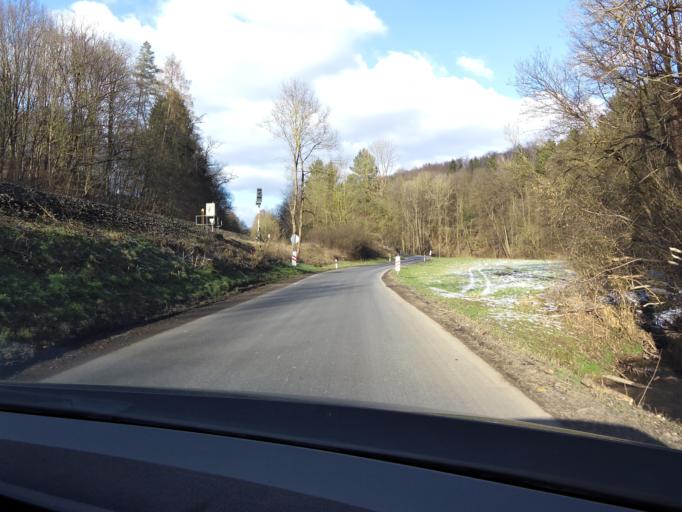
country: DE
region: Thuringia
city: Leimbach
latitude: 50.8399
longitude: 10.2064
